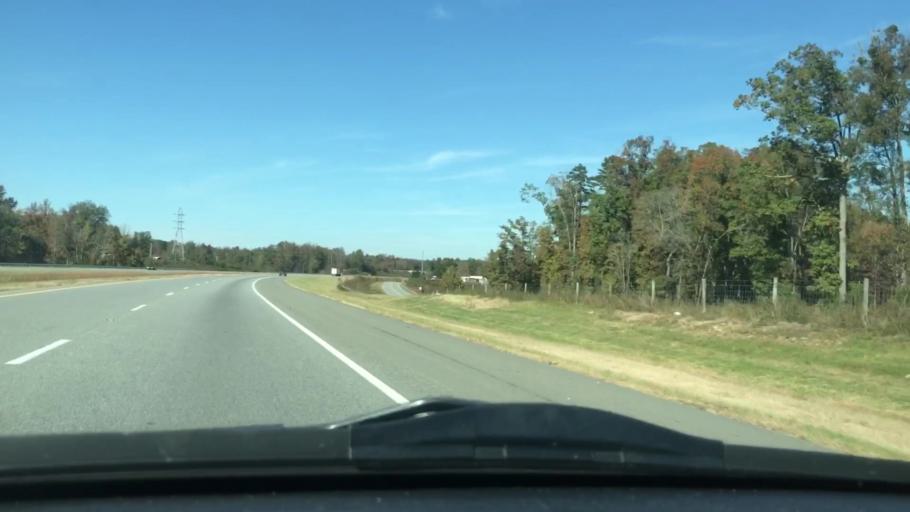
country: US
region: North Carolina
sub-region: Randolph County
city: Archdale
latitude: 35.8823
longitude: -79.9118
